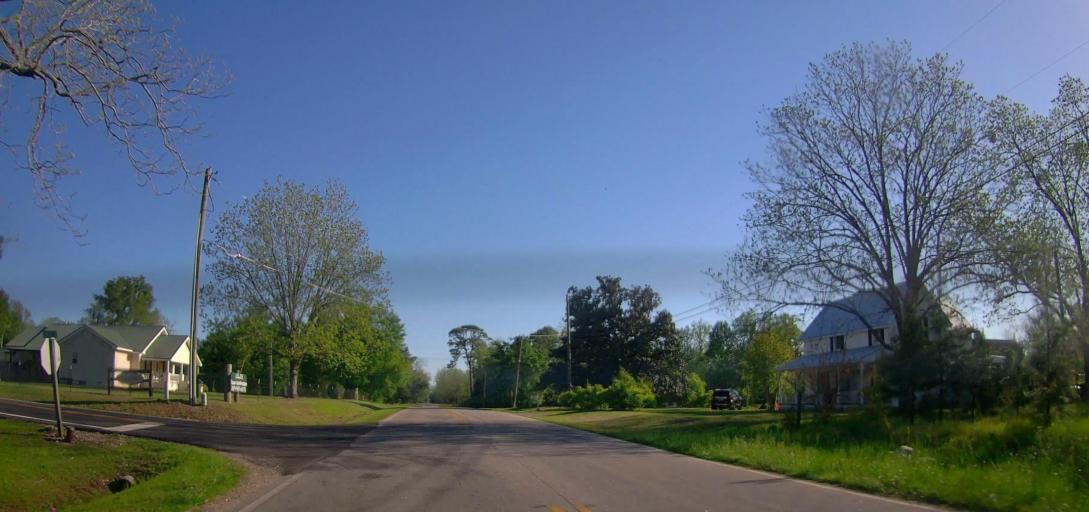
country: US
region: Georgia
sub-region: Ben Hill County
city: Fitzgerald
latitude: 31.7256
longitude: -83.2354
